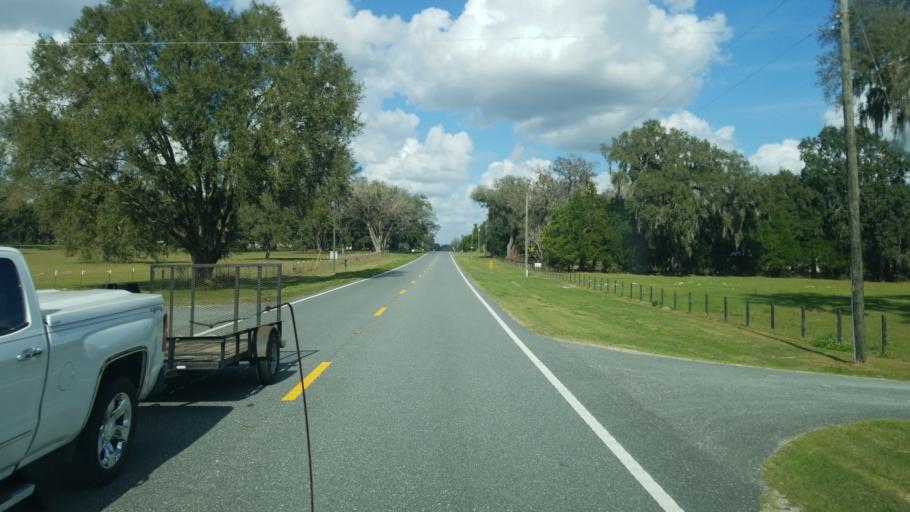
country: US
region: Florida
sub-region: Sumter County
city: Wildwood
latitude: 28.9162
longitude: -82.1200
